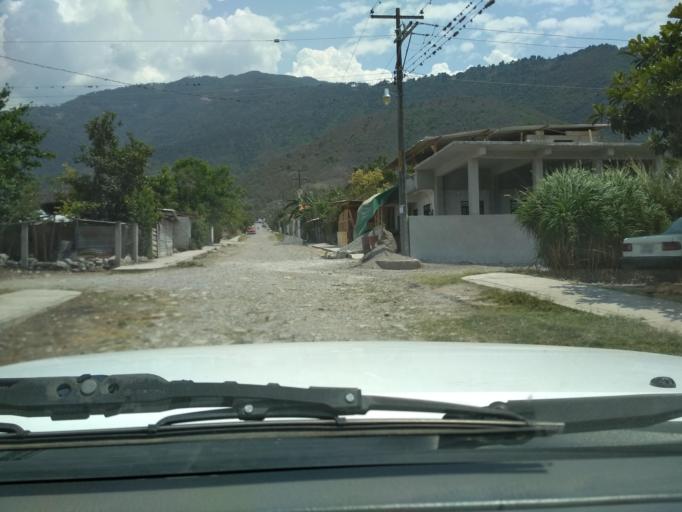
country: MX
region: Veracruz
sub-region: Acultzingo
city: Acatla
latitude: 18.7506
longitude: -97.2202
